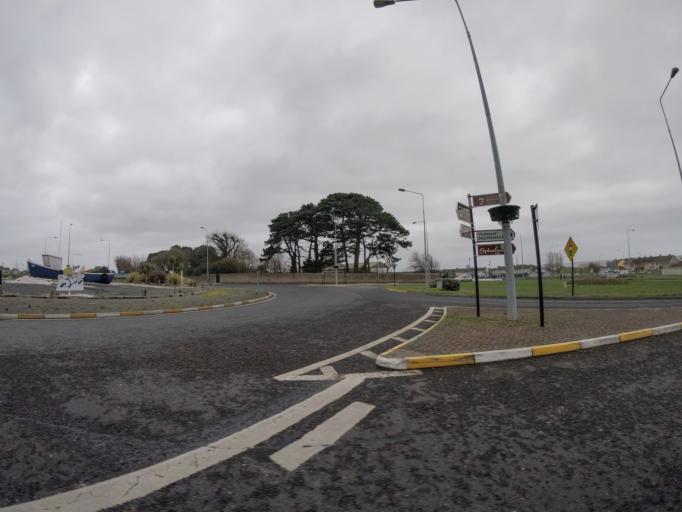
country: IE
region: Munster
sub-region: Waterford
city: Tra Mhor
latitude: 52.1685
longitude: -7.1439
